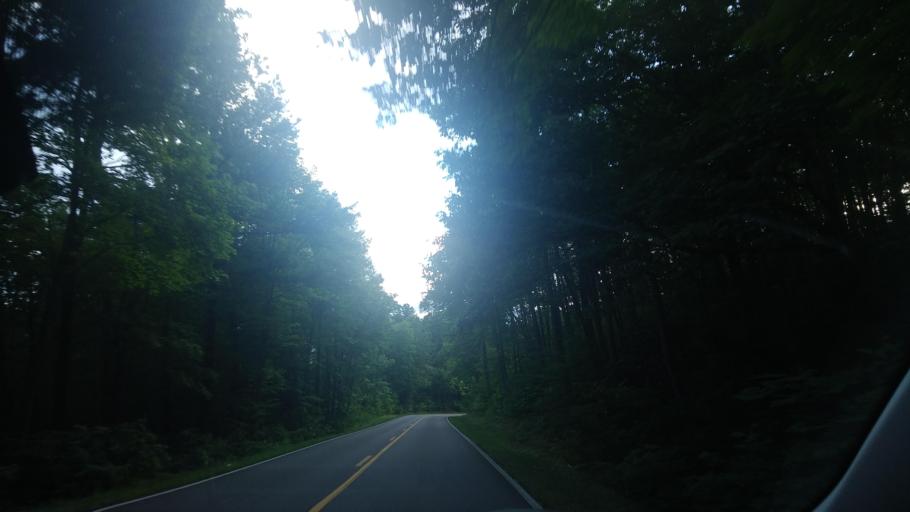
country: US
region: Tennessee
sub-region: Cocke County
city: Newport
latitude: 35.8264
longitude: -83.2025
